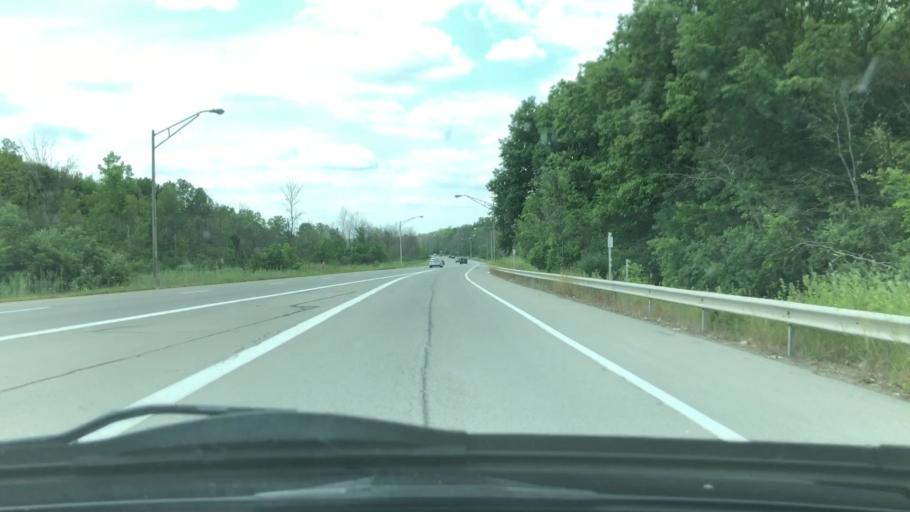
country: US
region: New York
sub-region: Monroe County
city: North Gates
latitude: 43.1210
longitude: -77.7491
